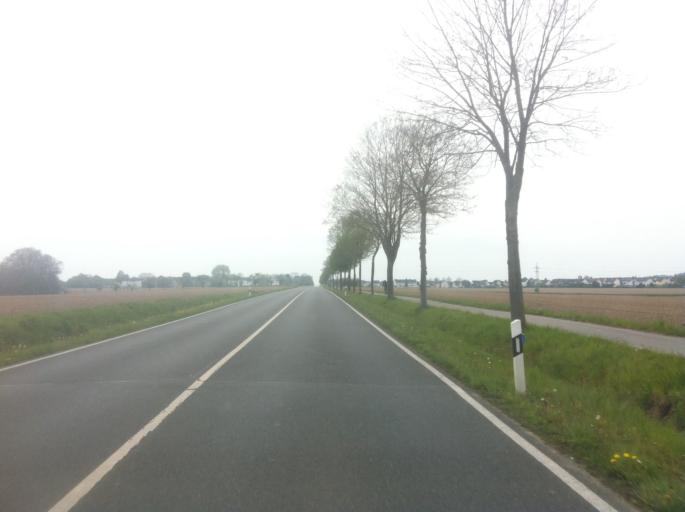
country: DE
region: North Rhine-Westphalia
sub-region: Regierungsbezirk Detmold
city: Lage
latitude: 52.0006
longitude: 8.8212
